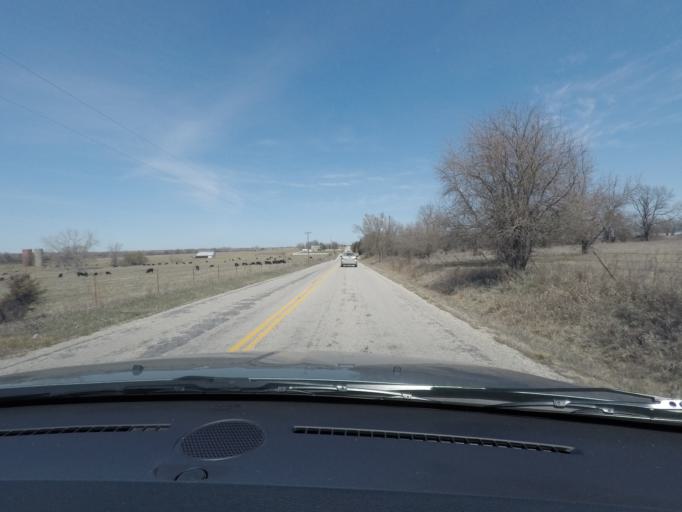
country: US
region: Kansas
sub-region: Lyon County
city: Emporia
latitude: 38.6107
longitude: -96.1697
